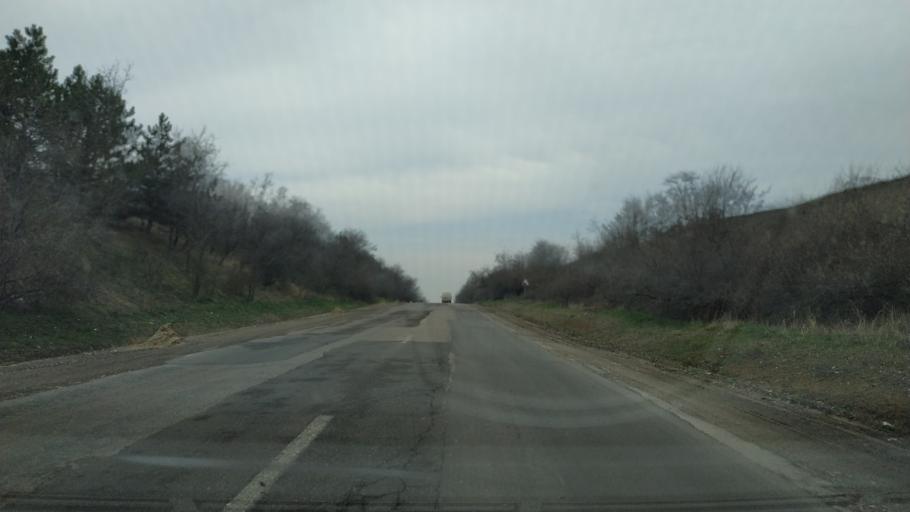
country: MD
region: Cahul
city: Cahul
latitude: 45.9579
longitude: 28.3698
